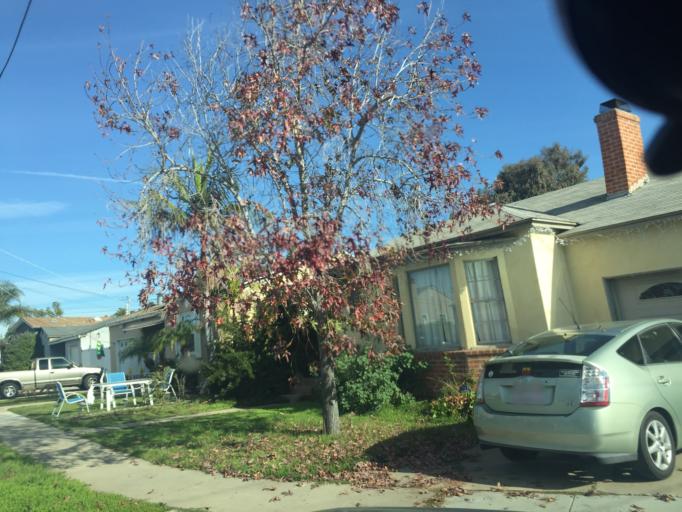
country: US
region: California
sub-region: San Diego County
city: Lemon Grove
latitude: 32.7616
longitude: -117.0801
